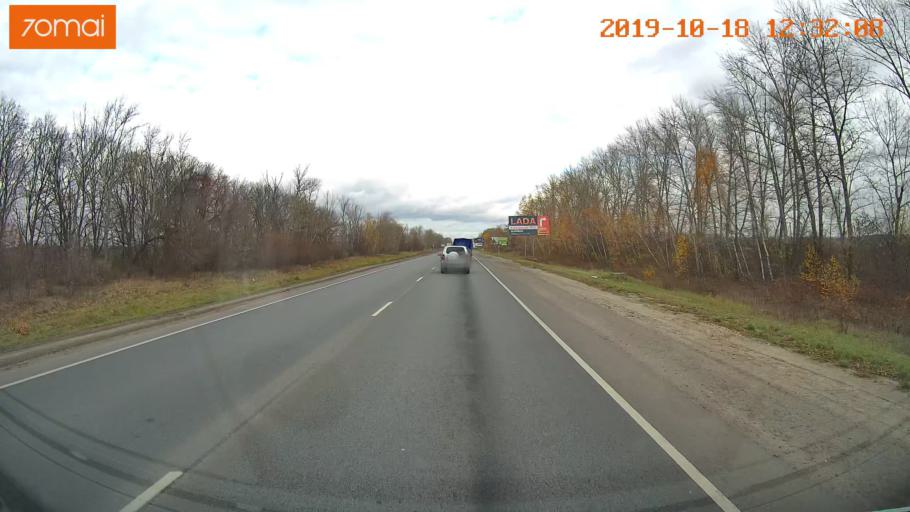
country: RU
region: Rjazan
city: Ryazan'
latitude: 54.5986
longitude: 39.6213
